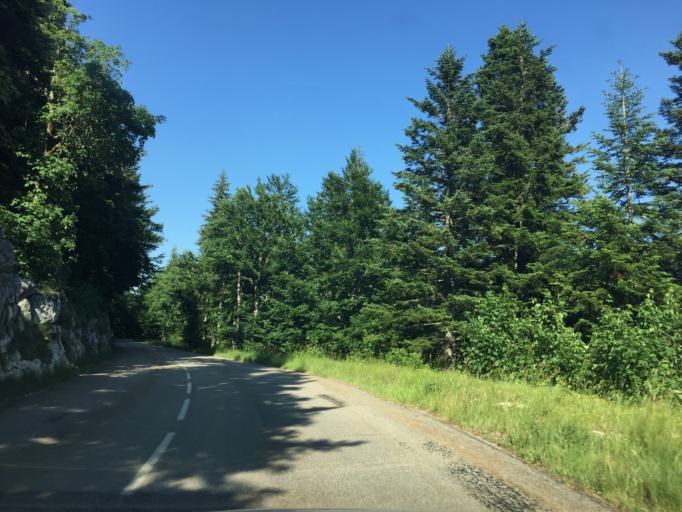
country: FR
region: Rhone-Alpes
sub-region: Departement de la Drome
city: Saint-Jean-en-Royans
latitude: 44.9616
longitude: 5.3309
